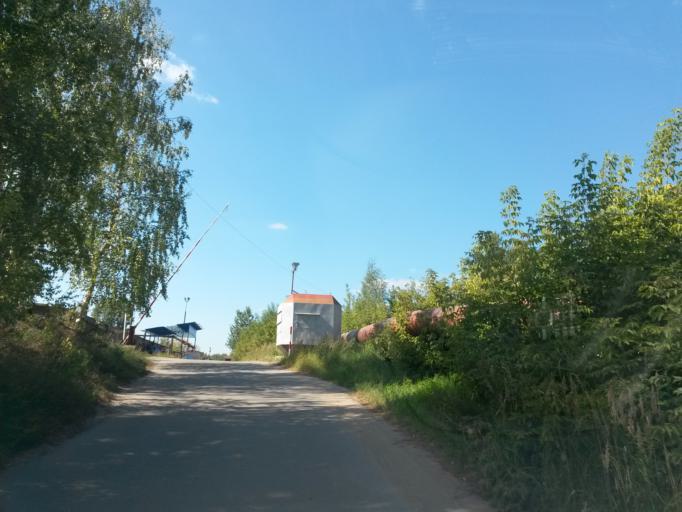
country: RU
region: Jaroslavl
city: Yaroslavl
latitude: 57.5763
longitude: 39.8402
